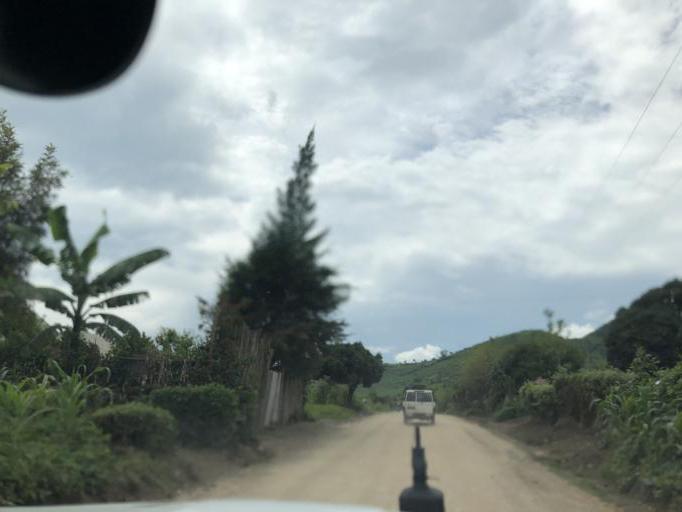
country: CD
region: Nord Kivu
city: Sake
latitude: -1.6641
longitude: 29.0195
